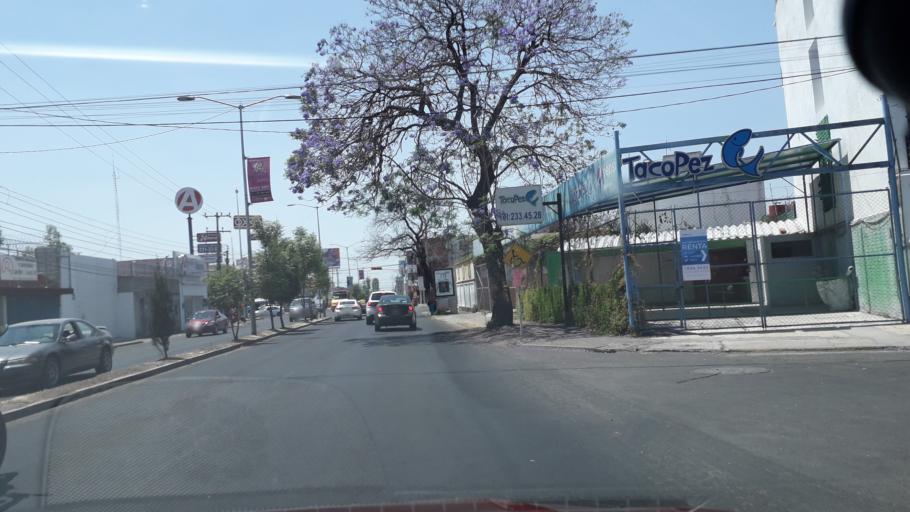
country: MX
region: Puebla
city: Puebla
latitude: 19.0218
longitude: -98.1920
